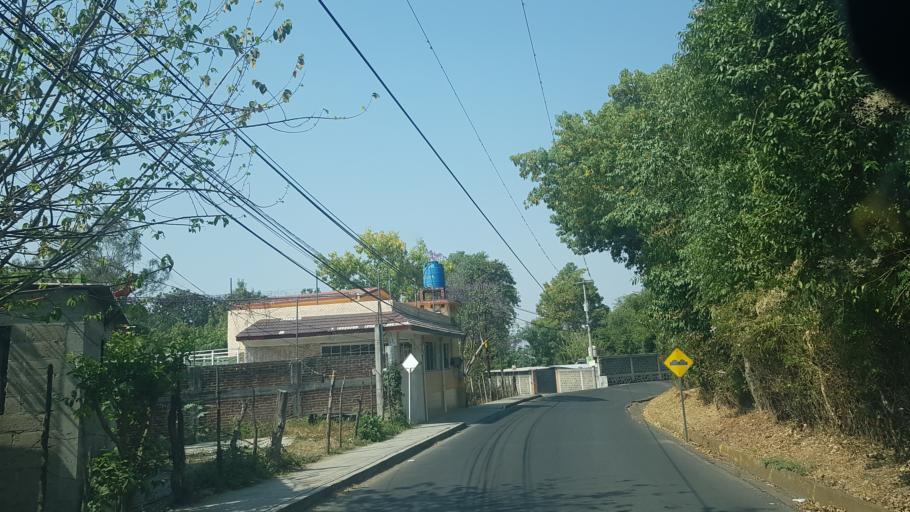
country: MX
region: Morelos
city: Tlacotepec
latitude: 18.8109
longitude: -98.7550
